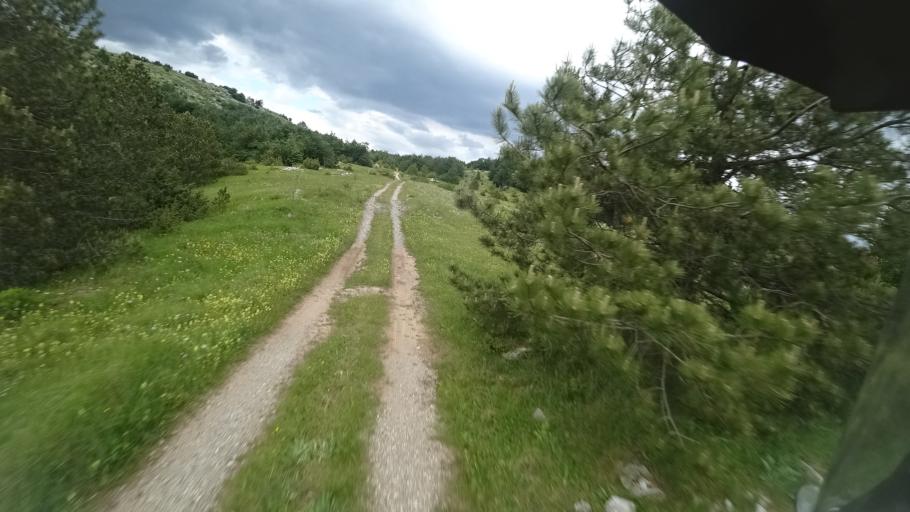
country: HR
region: Zadarska
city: Obrovac
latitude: 44.2740
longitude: 15.7446
